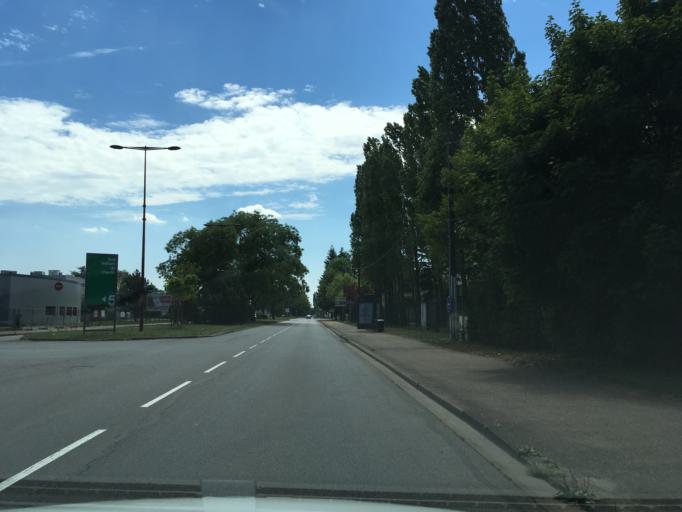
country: FR
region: Lorraine
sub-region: Departement de la Moselle
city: Woippy
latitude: 49.1450
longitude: 6.1718
